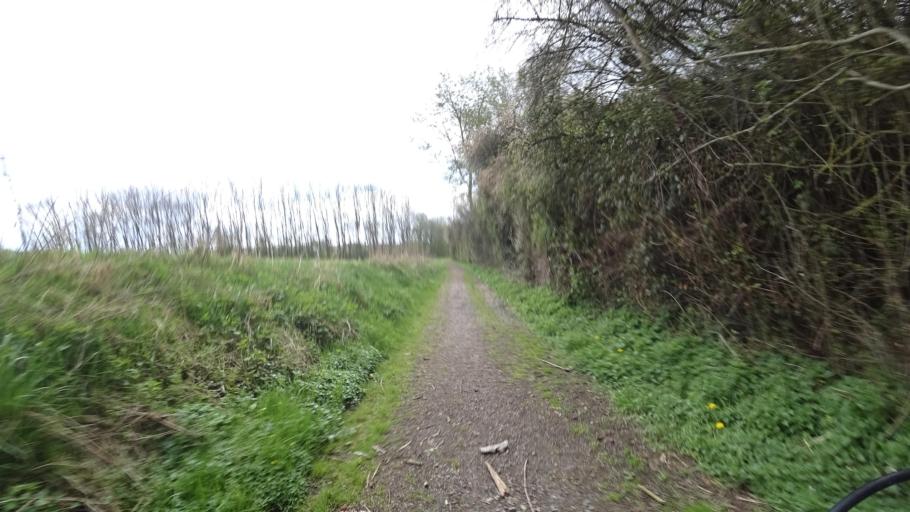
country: BE
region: Wallonia
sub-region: Province du Brabant Wallon
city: Walhain-Saint-Paul
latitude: 50.6335
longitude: 4.7287
